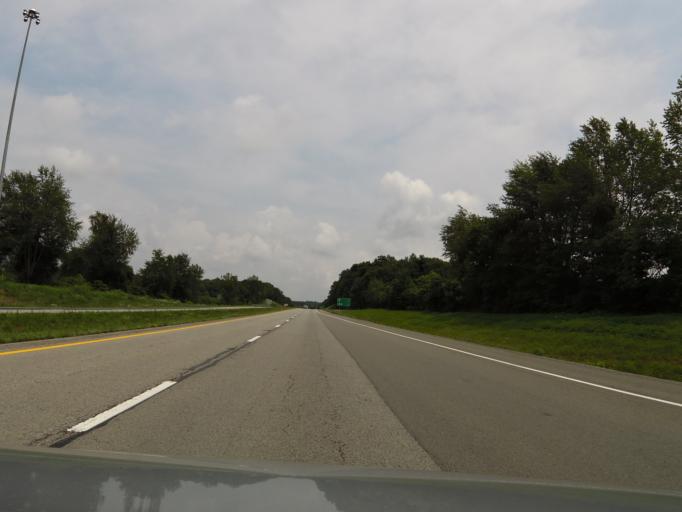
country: US
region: Kentucky
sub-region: Hardin County
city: Elizabethtown
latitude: 37.6591
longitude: -85.8854
